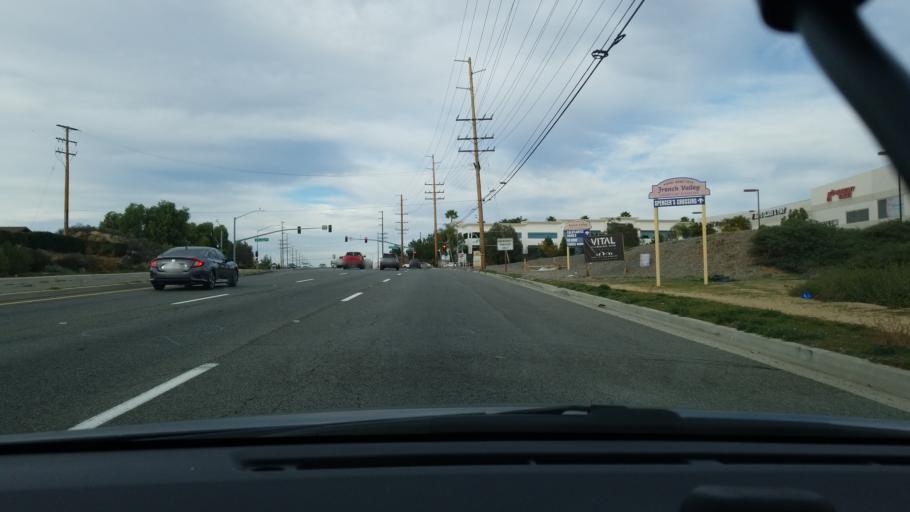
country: US
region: California
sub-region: Riverside County
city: Murrieta Hot Springs
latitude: 33.5595
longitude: -117.1391
